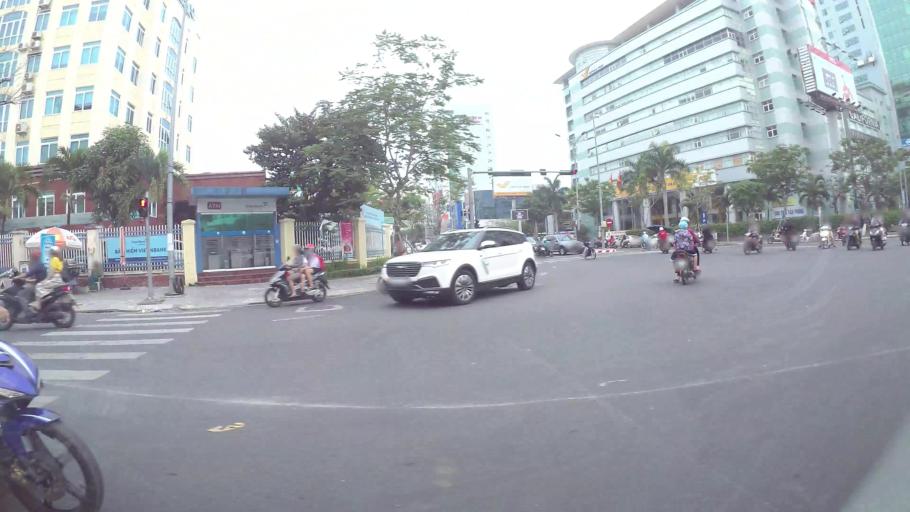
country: VN
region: Da Nang
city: Da Nang
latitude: 16.0602
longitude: 108.2111
